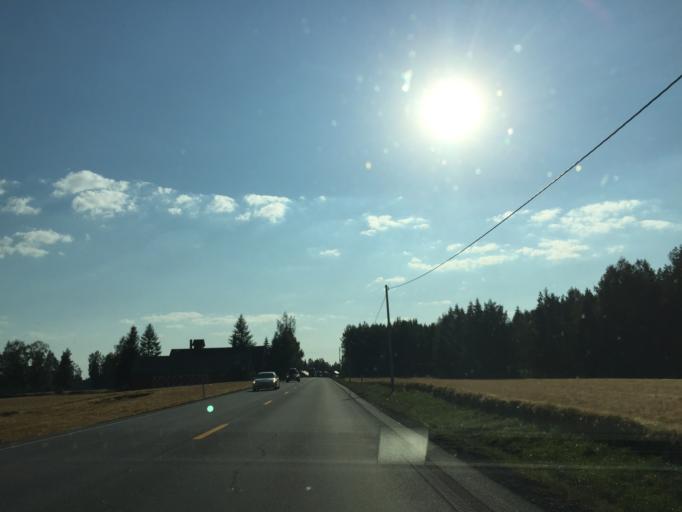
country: NO
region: Hedmark
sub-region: Sor-Odal
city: Skarnes
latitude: 60.2114
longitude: 11.6206
